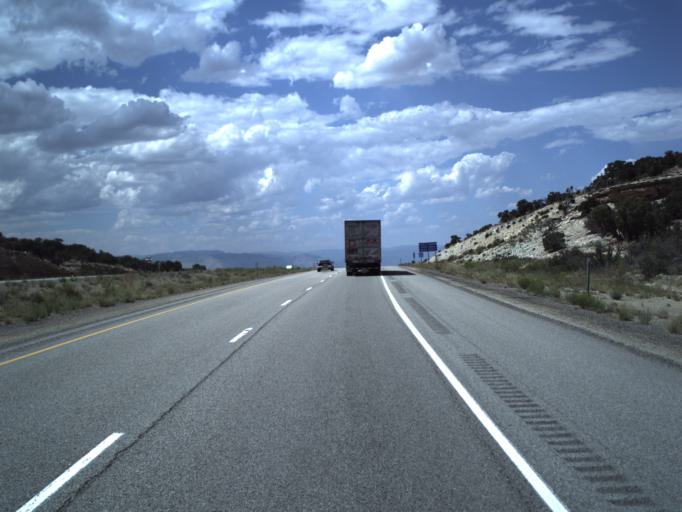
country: US
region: Utah
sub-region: Emery County
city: Ferron
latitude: 38.8504
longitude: -110.9050
